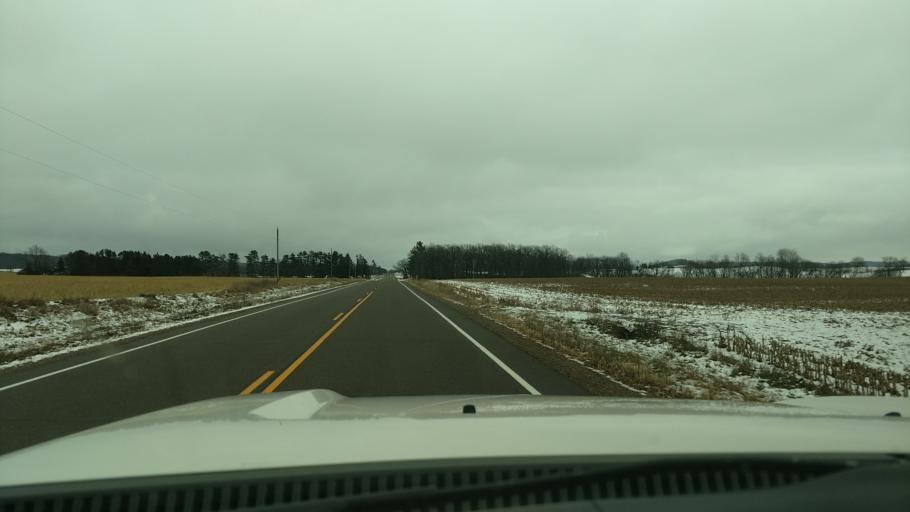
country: US
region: Wisconsin
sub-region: Dunn County
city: Colfax
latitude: 45.1427
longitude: -91.7010
